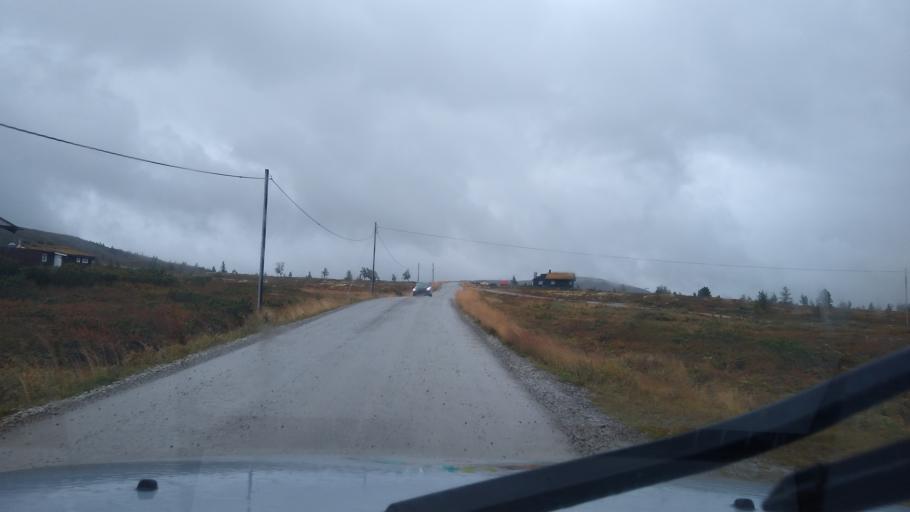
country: NO
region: Oppland
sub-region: Ringebu
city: Ringebu
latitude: 61.6716
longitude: 10.1061
